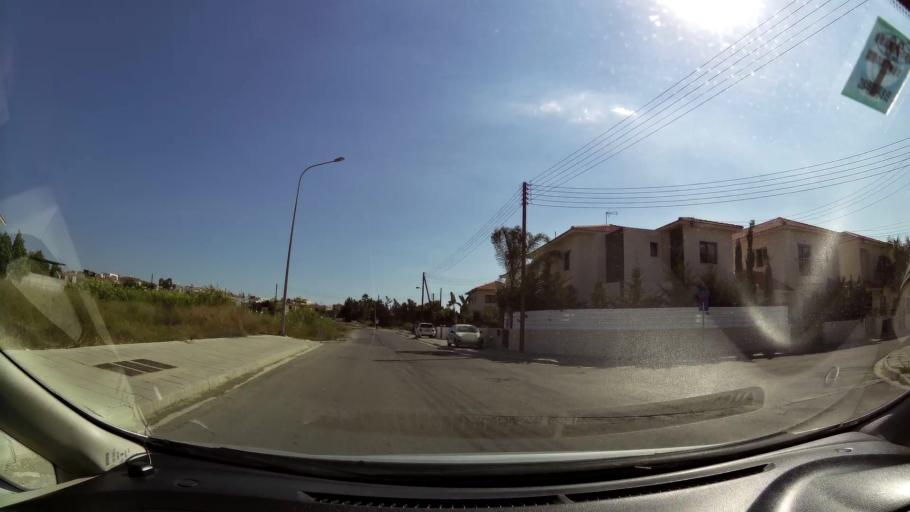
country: CY
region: Larnaka
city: Livadia
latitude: 34.9451
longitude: 33.6170
